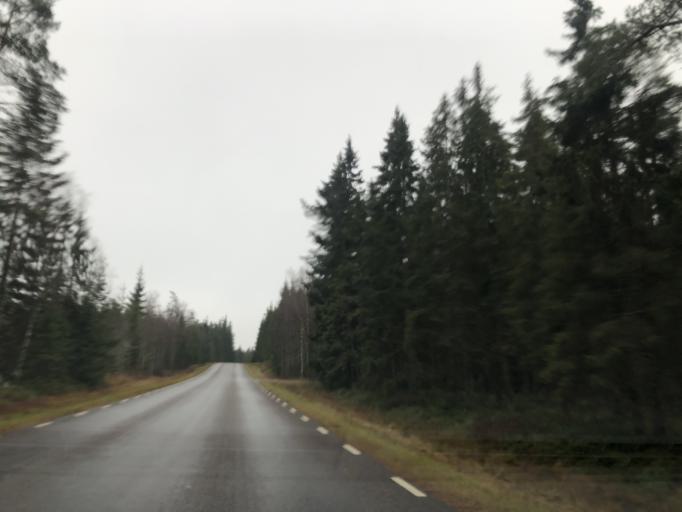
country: SE
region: Vaestra Goetaland
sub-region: Ulricehamns Kommun
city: Ulricehamn
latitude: 57.7406
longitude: 13.5384
